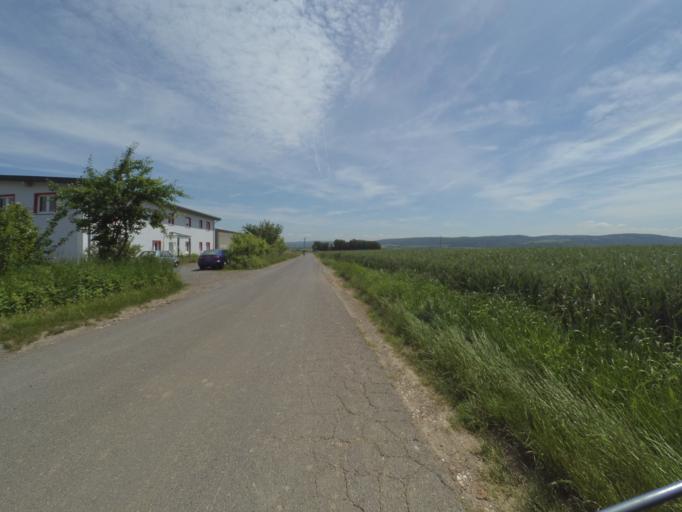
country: DE
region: Rheinland-Pfalz
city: Kobern-Gondorf
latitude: 50.3099
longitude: 7.4353
